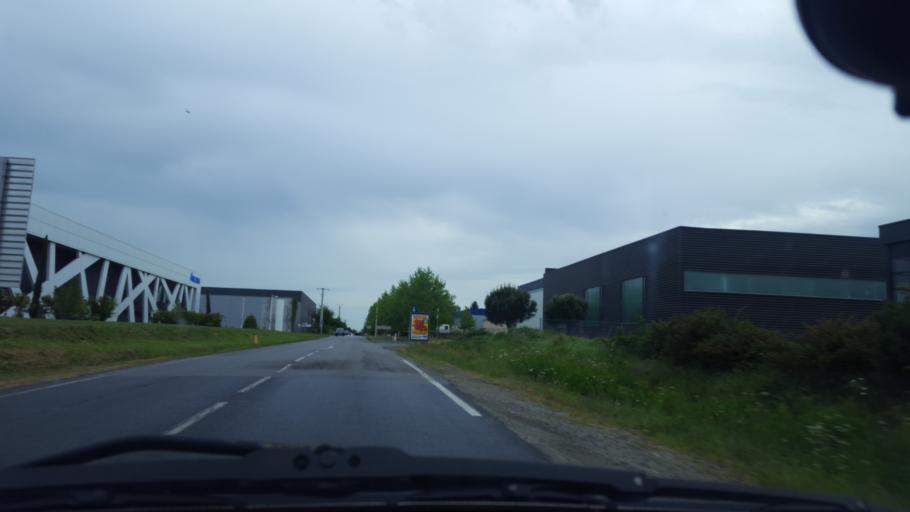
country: FR
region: Pays de la Loire
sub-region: Departement de la Loire-Atlantique
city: Les Sorinieres
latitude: 47.1345
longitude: -1.5196
